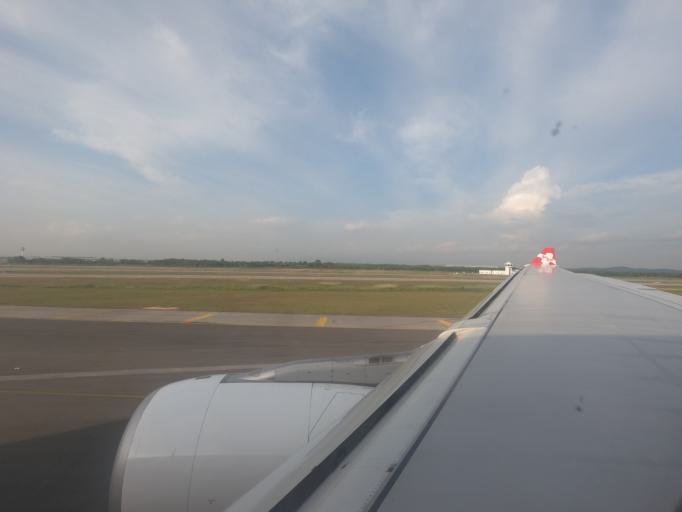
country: MY
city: Sungai Pelek New Village
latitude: 2.7252
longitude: 101.6863
